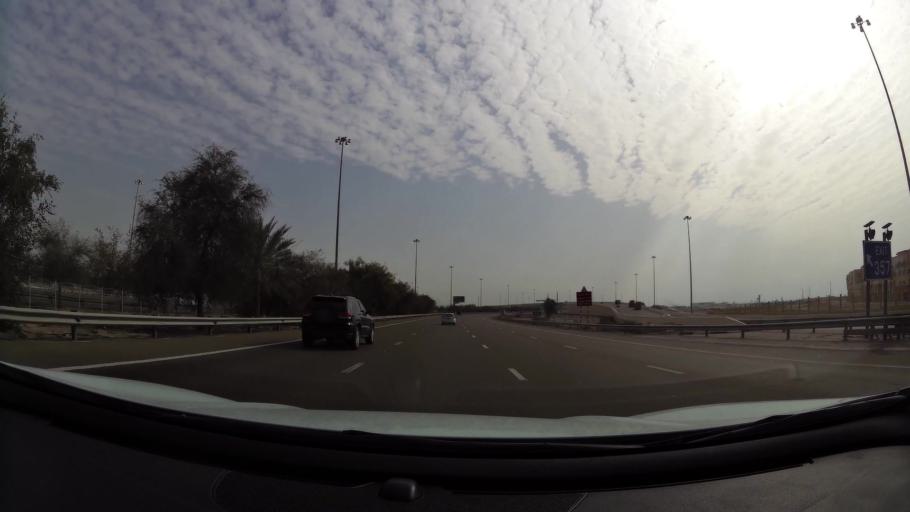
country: AE
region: Abu Dhabi
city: Abu Dhabi
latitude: 24.5510
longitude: 54.6943
